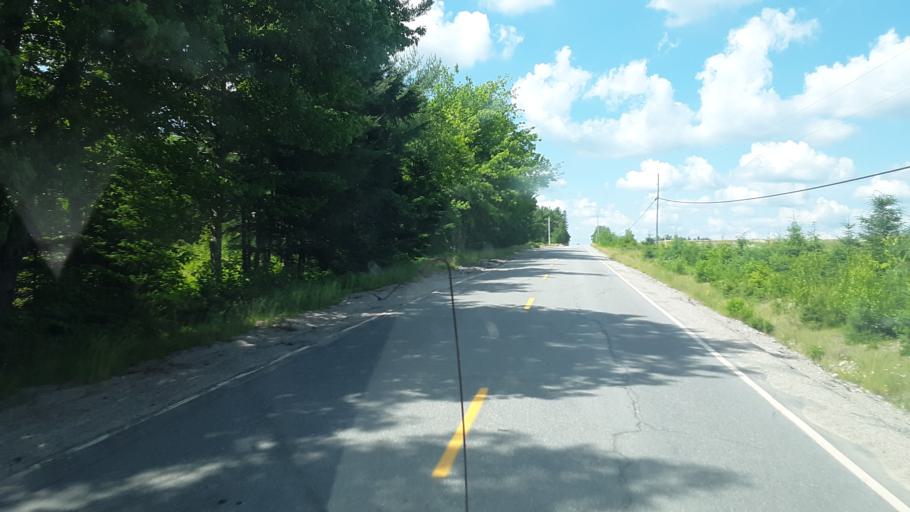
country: US
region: Maine
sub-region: Washington County
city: Machias
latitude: 44.9449
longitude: -67.6639
